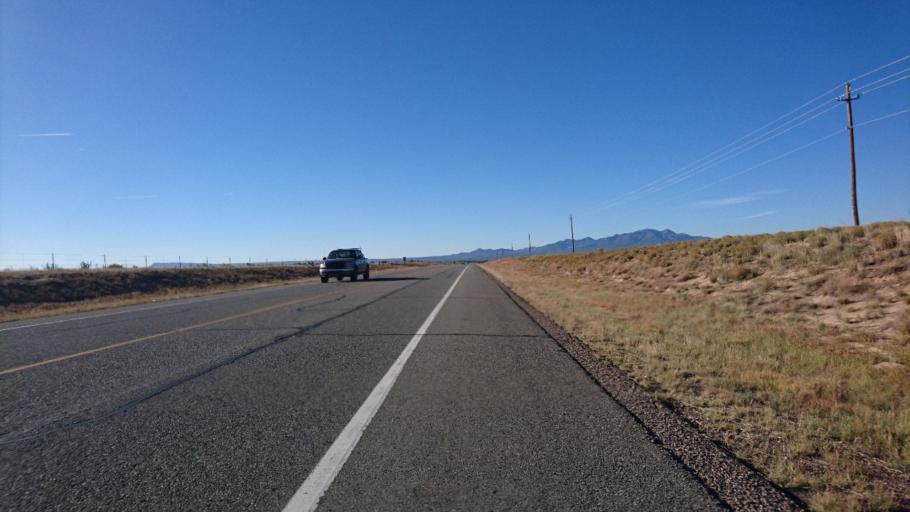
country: US
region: New Mexico
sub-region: Santa Fe County
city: La Cienega
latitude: 35.5091
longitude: -106.0622
